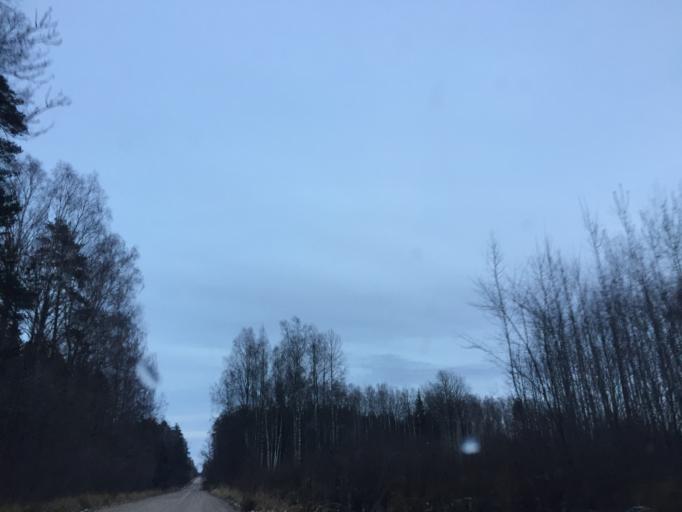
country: LV
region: Burtnieki
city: Matisi
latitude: 57.6315
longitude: 25.1324
